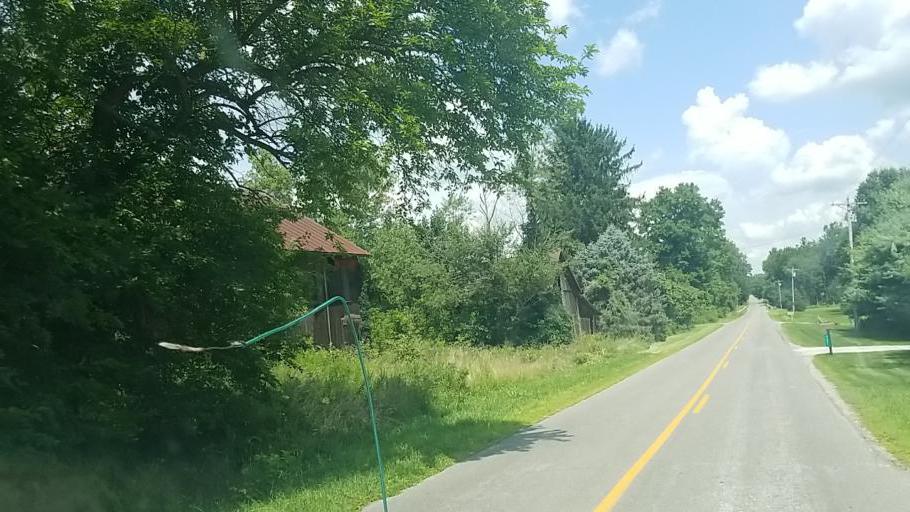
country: US
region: Ohio
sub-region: Medina County
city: Lodi
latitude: 41.0146
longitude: -82.0546
